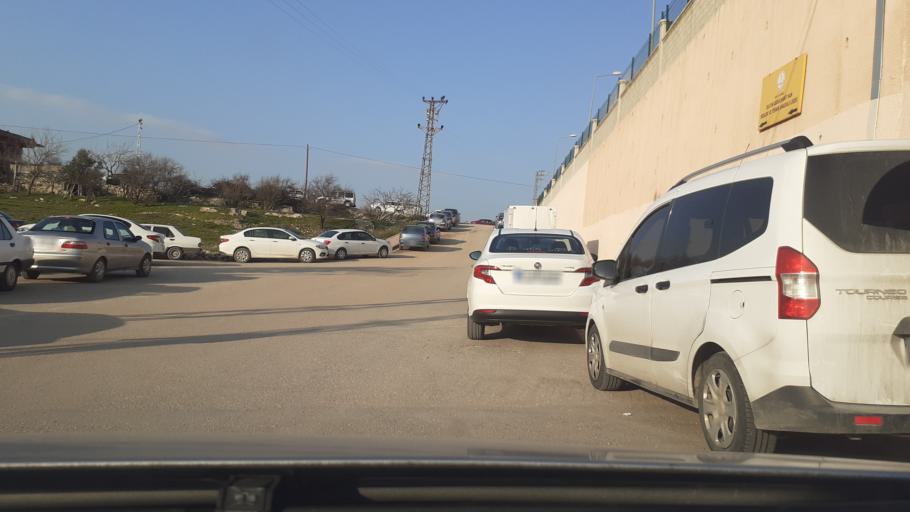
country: TR
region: Hatay
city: Fatikli
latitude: 36.1140
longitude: 36.2661
